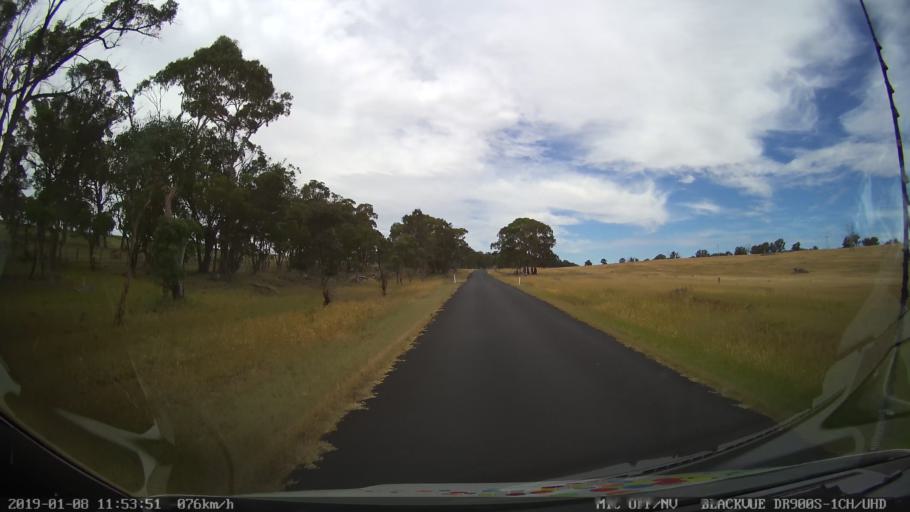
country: AU
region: New South Wales
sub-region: Armidale Dumaresq
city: Armidale
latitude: -30.4192
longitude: 151.5624
